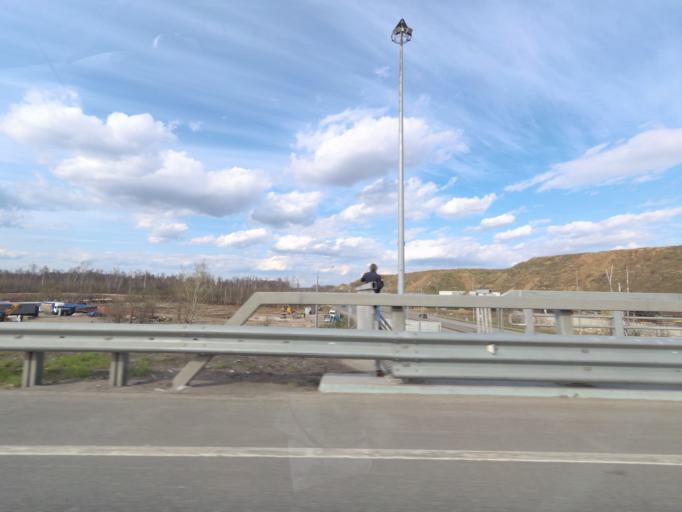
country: RU
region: Moscow
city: Businovo
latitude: 55.8946
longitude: 37.4953
